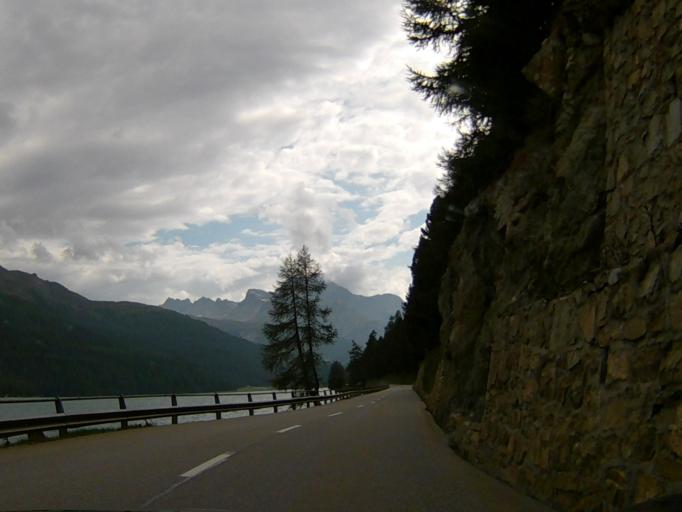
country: CH
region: Grisons
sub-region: Maloja District
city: Silvaplana
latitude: 46.4529
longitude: 9.7877
